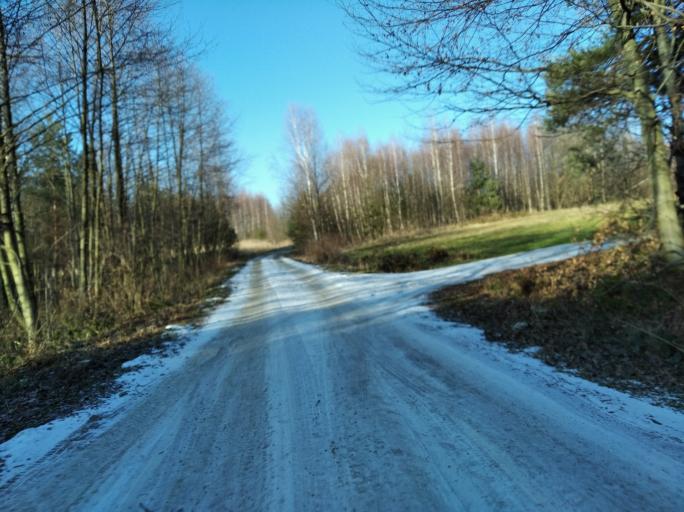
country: PL
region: Subcarpathian Voivodeship
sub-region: Powiat strzyzowski
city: Jawornik
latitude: 49.8353
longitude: 21.8582
